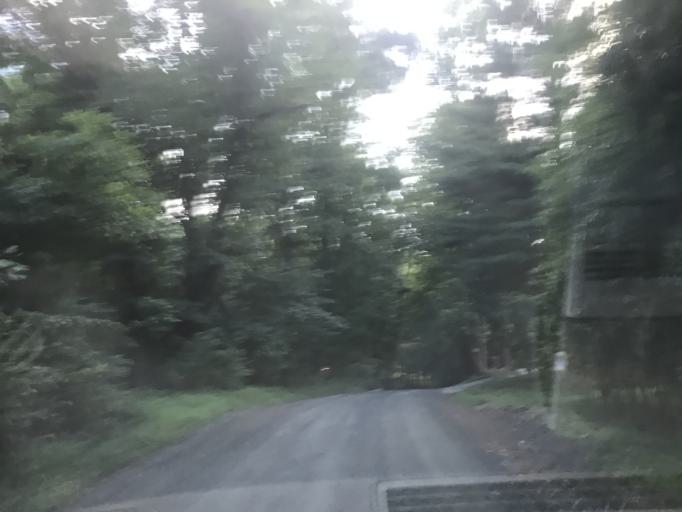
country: US
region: Maryland
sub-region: Harford County
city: Bel Air South
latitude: 39.5025
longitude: -76.2816
